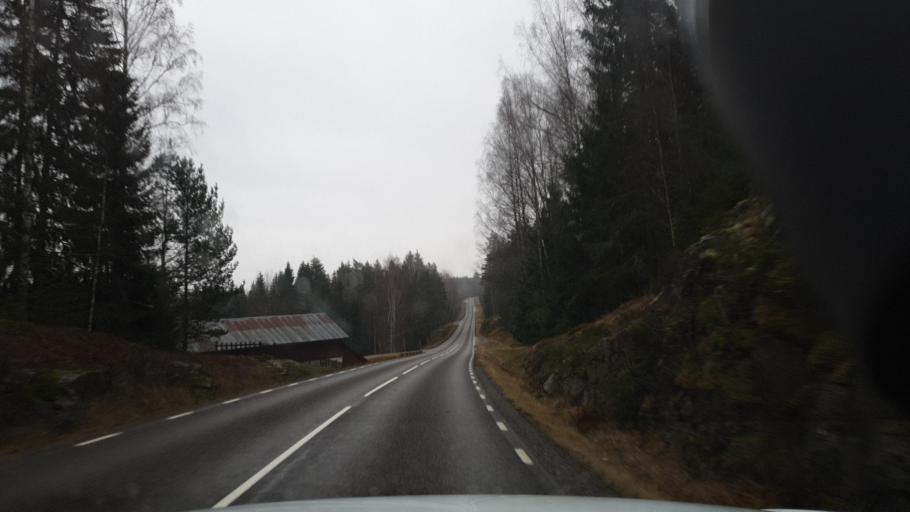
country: SE
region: Vaermland
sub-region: Eda Kommun
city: Amotfors
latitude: 59.7359
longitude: 12.4069
